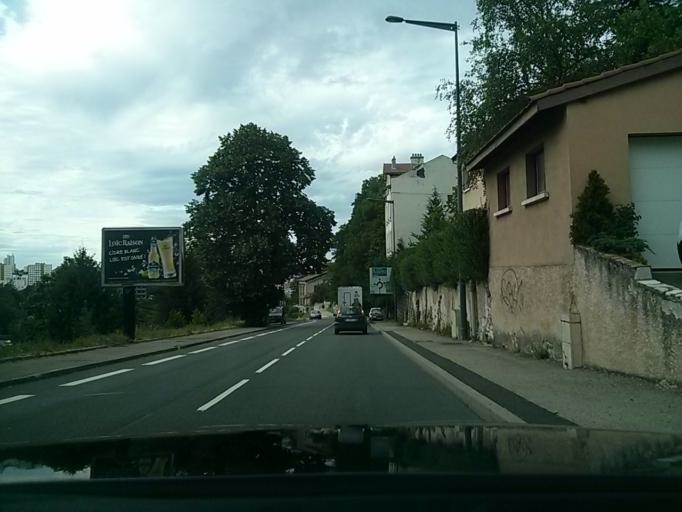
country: FR
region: Rhone-Alpes
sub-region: Departement de la Loire
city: Saint-Etienne
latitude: 45.4076
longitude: 4.4004
